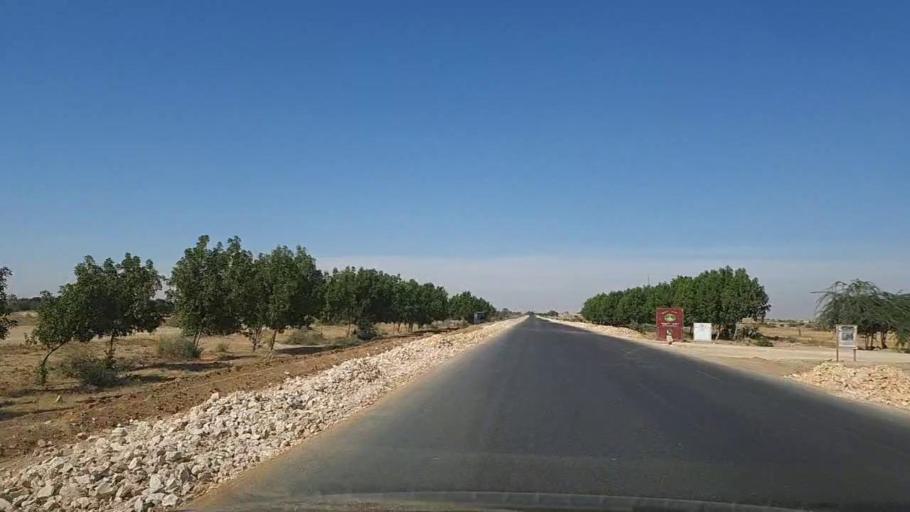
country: PK
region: Sindh
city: Kotri
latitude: 25.2731
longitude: 68.2160
